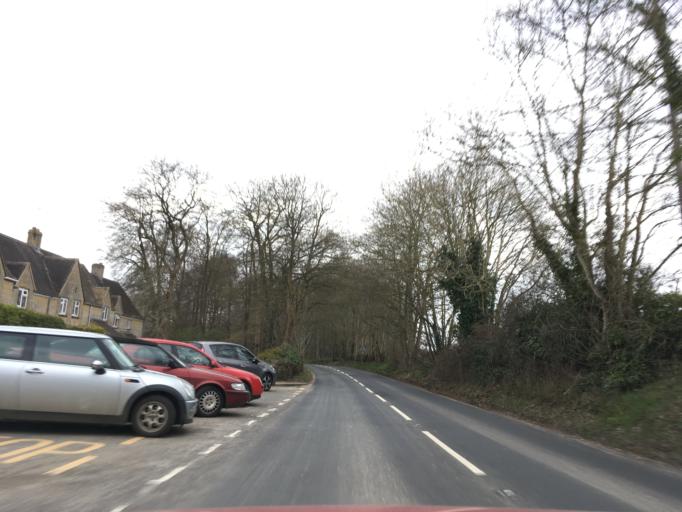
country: GB
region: England
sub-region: Gloucestershire
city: Northleach
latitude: 51.7635
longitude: -1.8263
